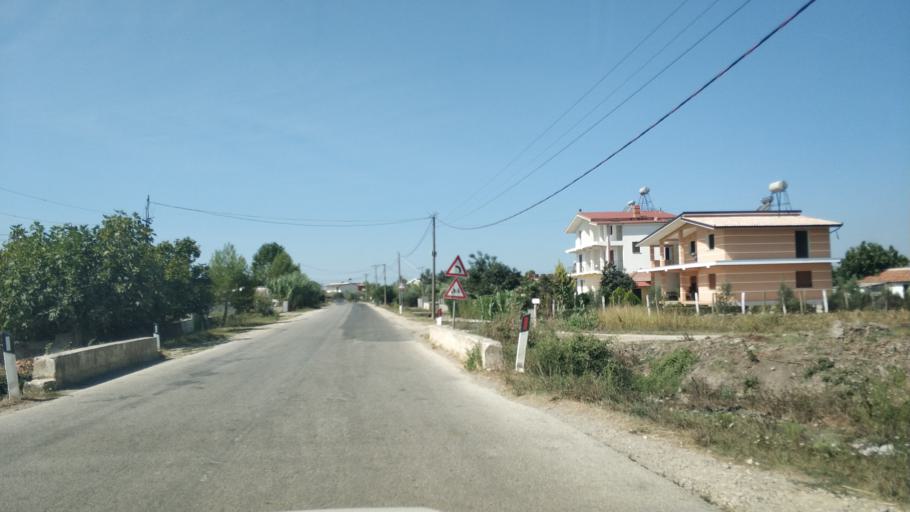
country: AL
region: Fier
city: Terbuf
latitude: 41.0520
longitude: 19.5846
